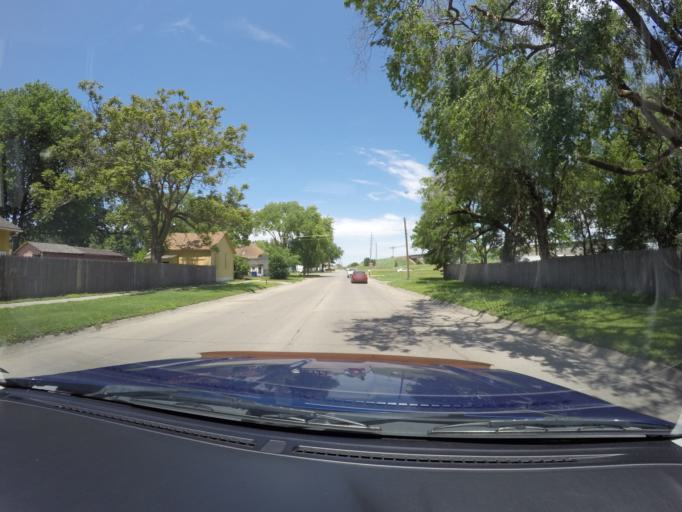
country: US
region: Nebraska
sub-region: Hall County
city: Grand Island
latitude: 40.9257
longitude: -98.3328
